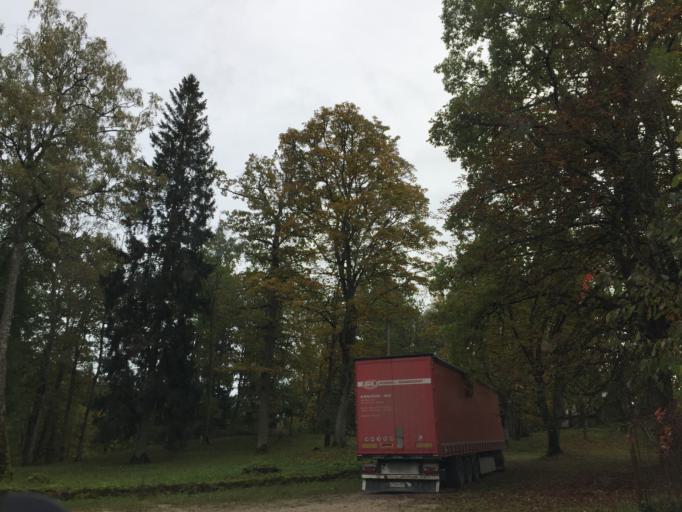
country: LV
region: Auces Novads
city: Auce
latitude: 56.5506
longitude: 23.0182
